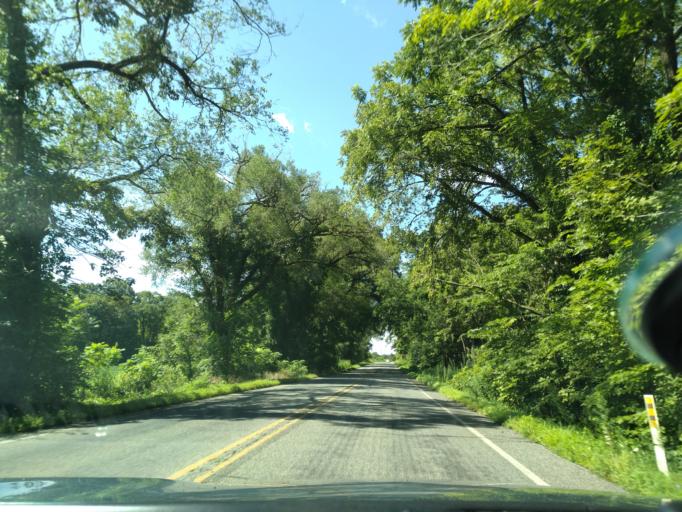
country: US
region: Pennsylvania
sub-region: Pike County
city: Pocono Ranch Lands
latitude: 41.1271
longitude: -74.9511
